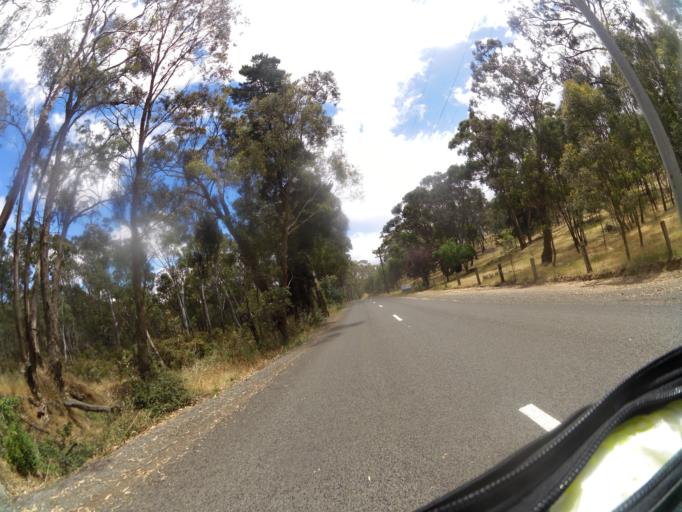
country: AU
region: Victoria
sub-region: Mount Alexander
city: Castlemaine
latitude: -37.0302
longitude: 144.2456
